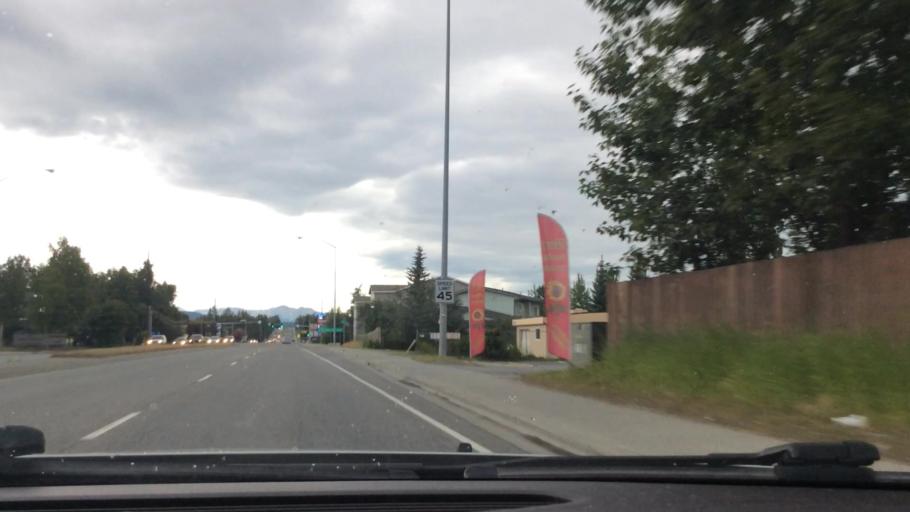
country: US
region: Alaska
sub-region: Anchorage Municipality
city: Anchorage
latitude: 61.1981
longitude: -149.7785
